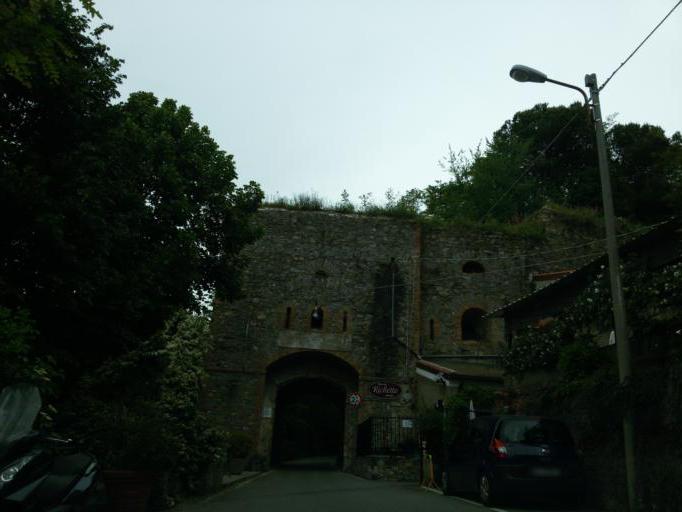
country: IT
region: Liguria
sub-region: Provincia di Genova
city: Genoa
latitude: 44.4304
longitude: 8.9320
